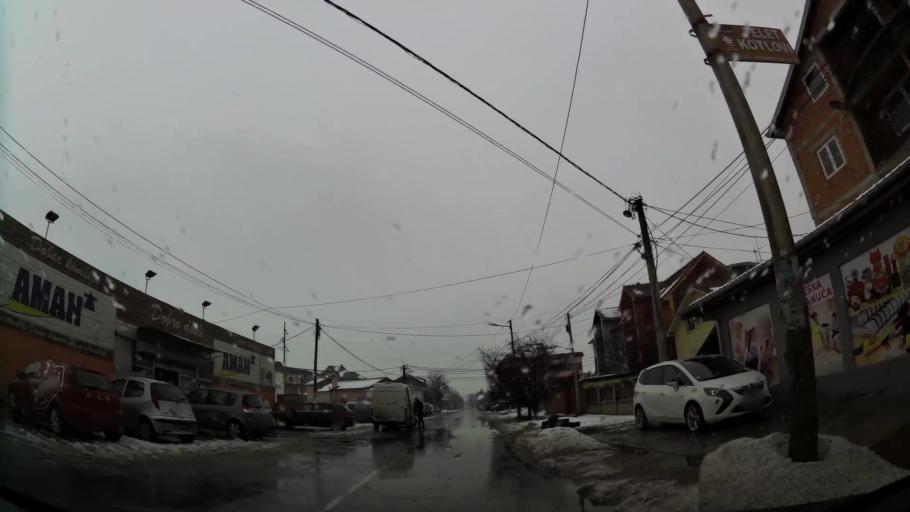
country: RS
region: Central Serbia
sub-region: Belgrade
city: Zemun
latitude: 44.8544
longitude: 20.3609
